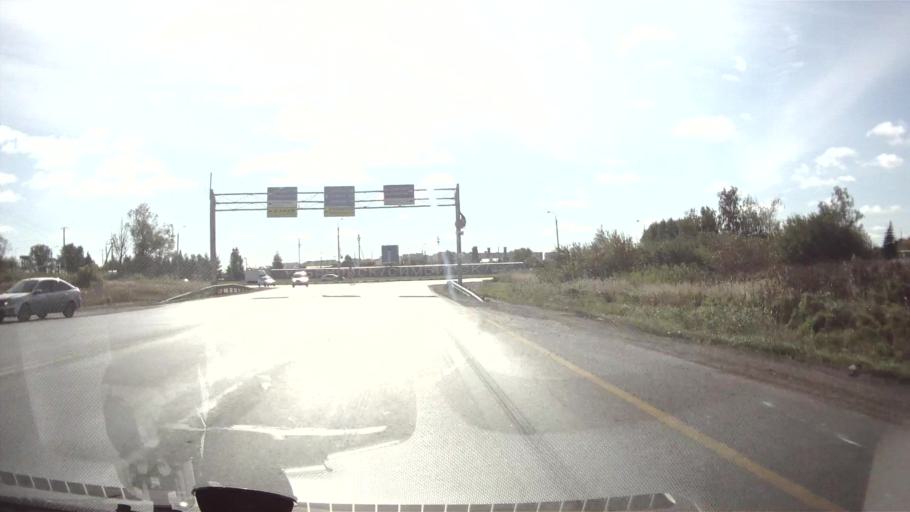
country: RU
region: Ulyanovsk
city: Isheyevka
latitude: 54.2924
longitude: 48.2531
